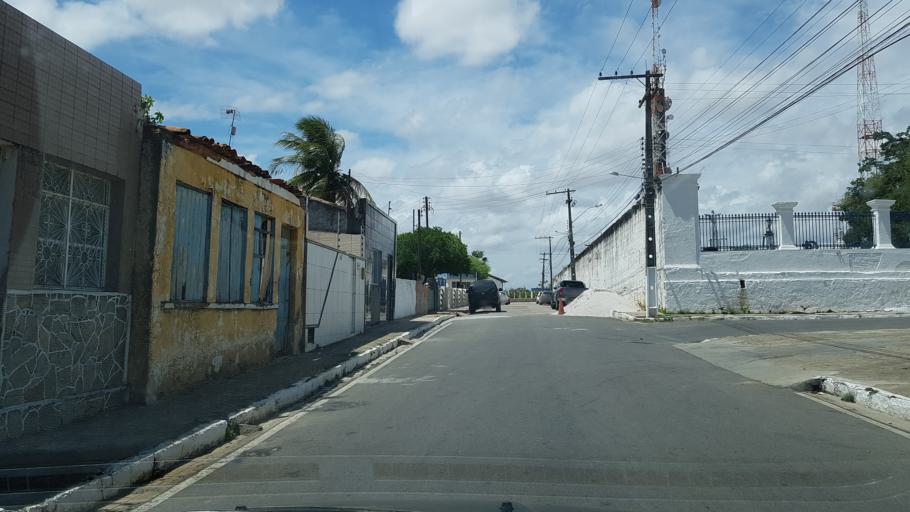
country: BR
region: Alagoas
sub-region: Penedo
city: Penedo
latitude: -10.2836
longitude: -36.5737
